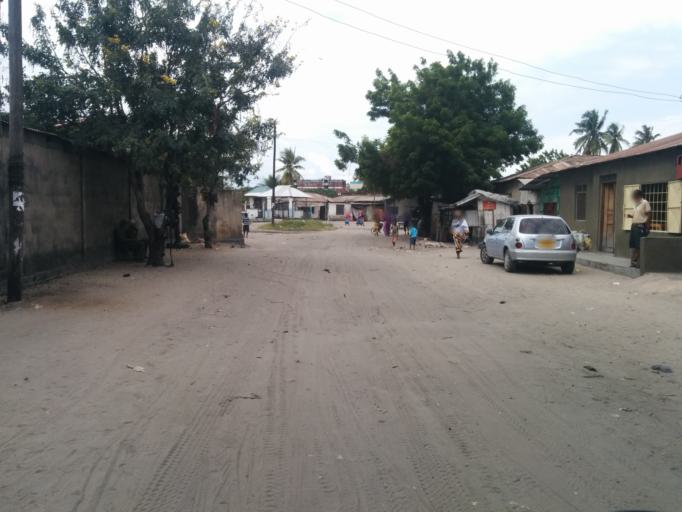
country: TZ
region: Dar es Salaam
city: Dar es Salaam
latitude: -6.8628
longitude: 39.2539
